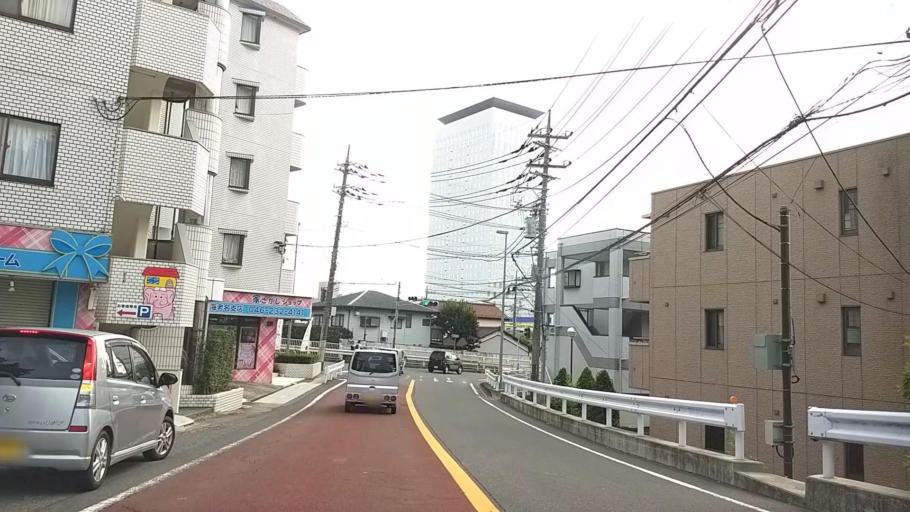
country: JP
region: Kanagawa
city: Zama
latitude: 35.4519
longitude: 139.3975
